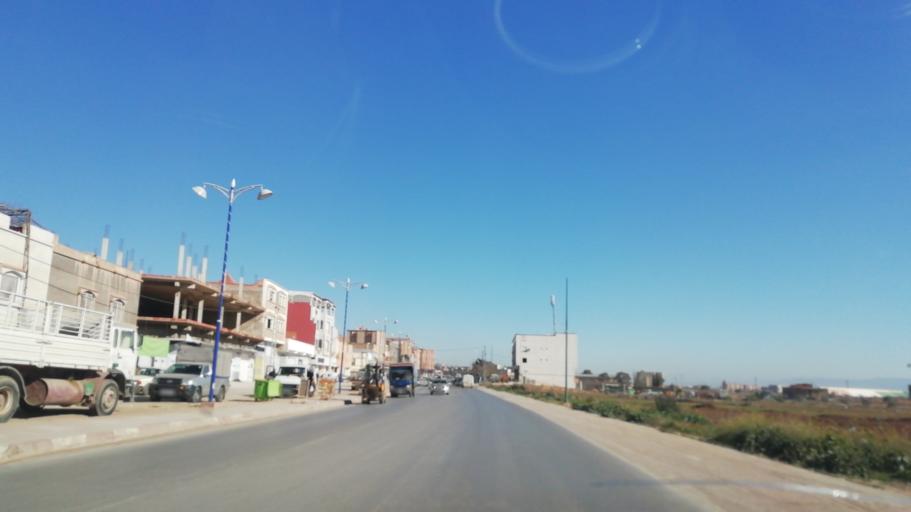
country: DZ
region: Tlemcen
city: Nedroma
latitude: 34.8423
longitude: -1.7625
